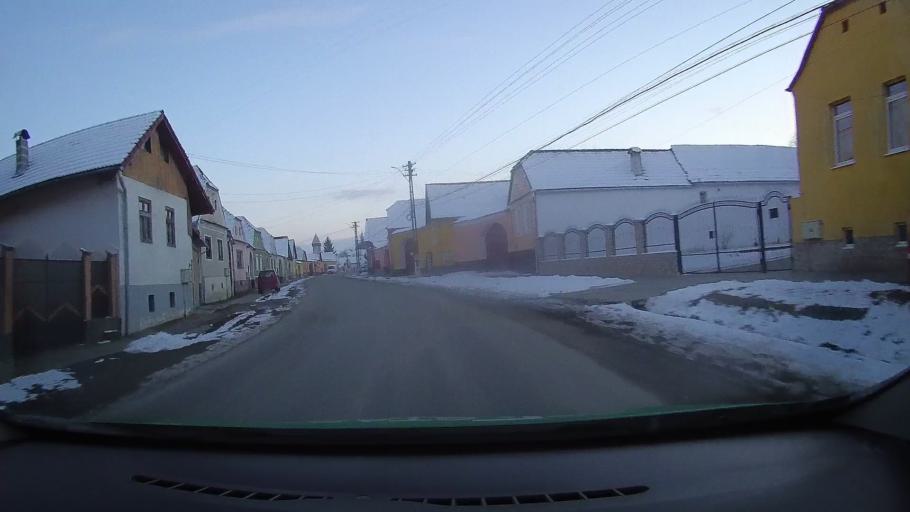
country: RO
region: Sibiu
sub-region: Comuna Brateiu
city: Brateiu
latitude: 46.1962
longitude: 24.4431
